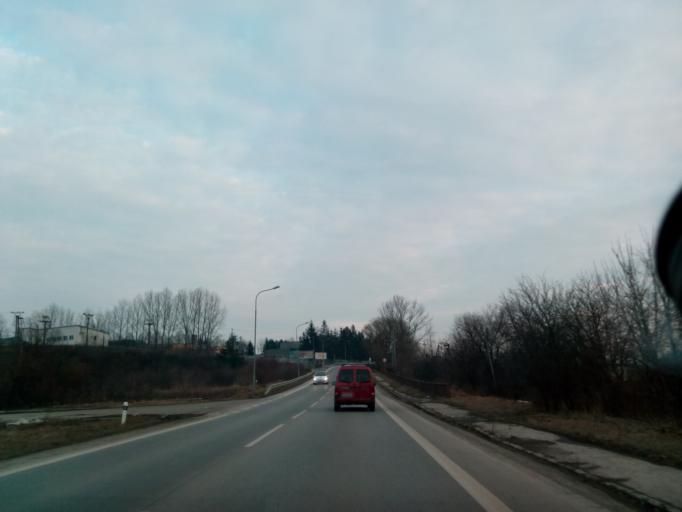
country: SK
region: Presovsky
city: Sabinov
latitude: 49.1136
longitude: 21.0771
